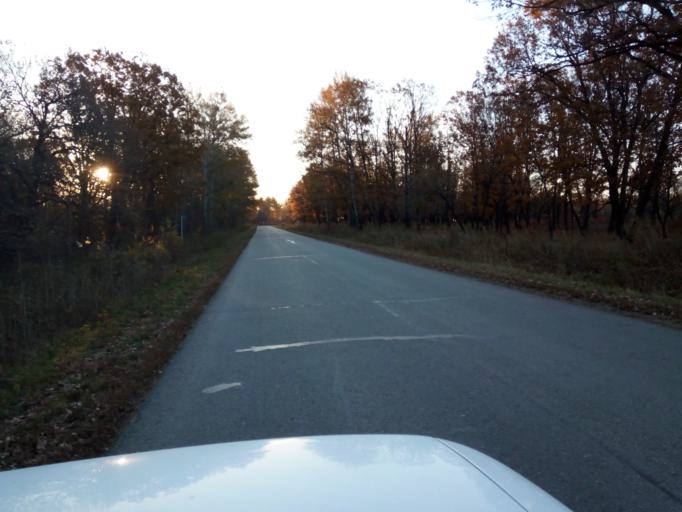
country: RU
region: Primorskiy
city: Lazo
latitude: 45.8715
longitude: 133.6575
